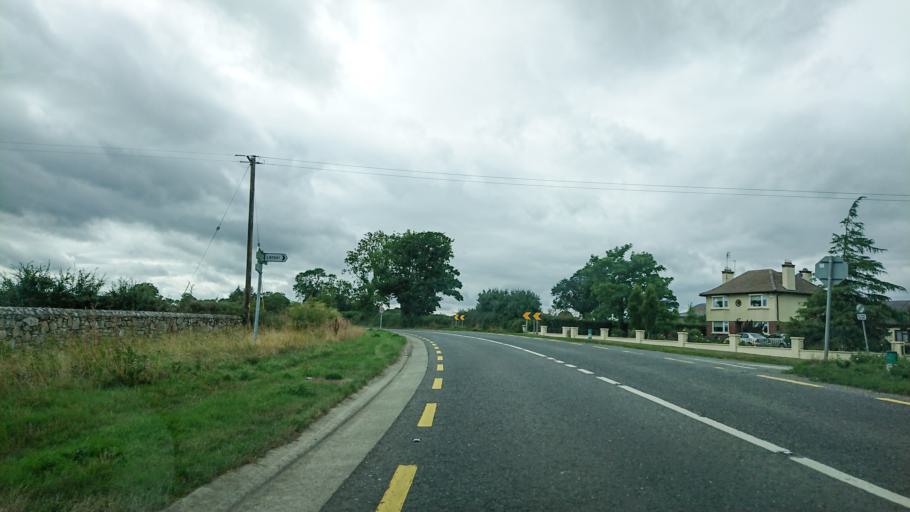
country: IE
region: Munster
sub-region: County Cork
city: Mallow
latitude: 52.1548
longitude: -8.5627
